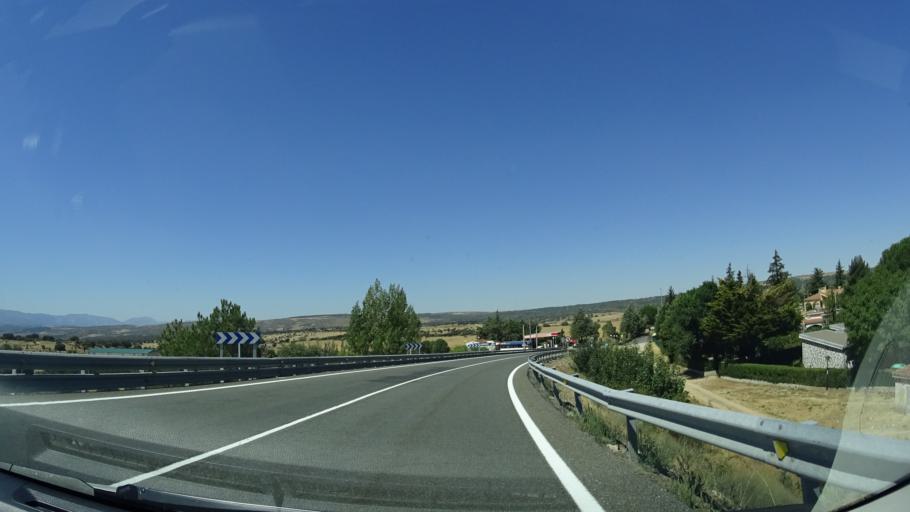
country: ES
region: Castille and Leon
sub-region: Provincia de Avila
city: Navalperal de Pinares
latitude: 40.5854
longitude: -4.4081
